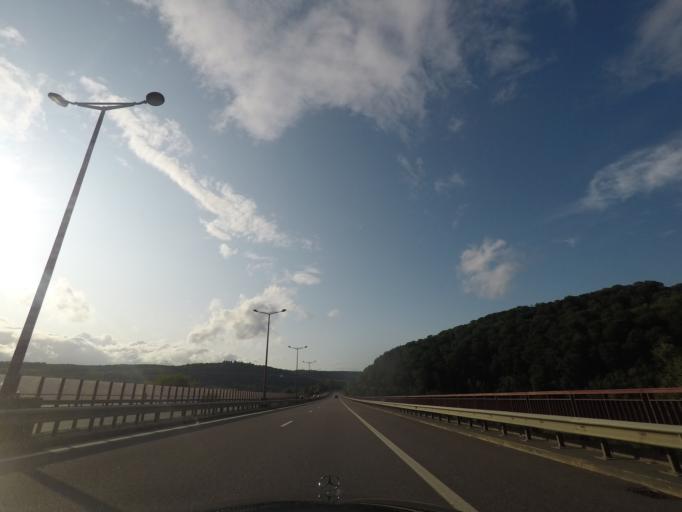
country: LU
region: Luxembourg
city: Colmar
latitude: 49.8127
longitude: 6.1048
